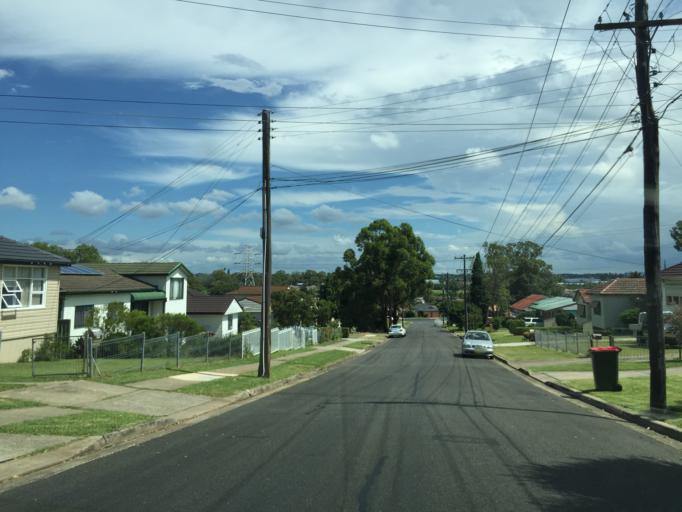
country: AU
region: New South Wales
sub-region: Blacktown
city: Doonside
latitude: -33.7802
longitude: 150.8902
